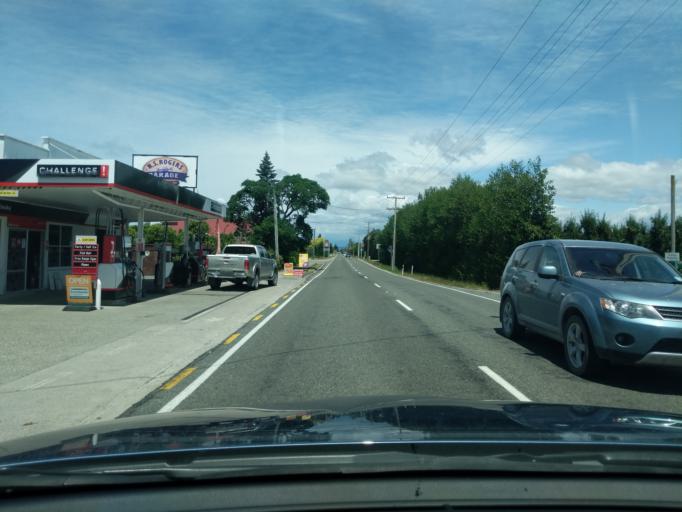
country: NZ
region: Tasman
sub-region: Tasman District
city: Motueka
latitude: -41.0850
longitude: 172.9970
